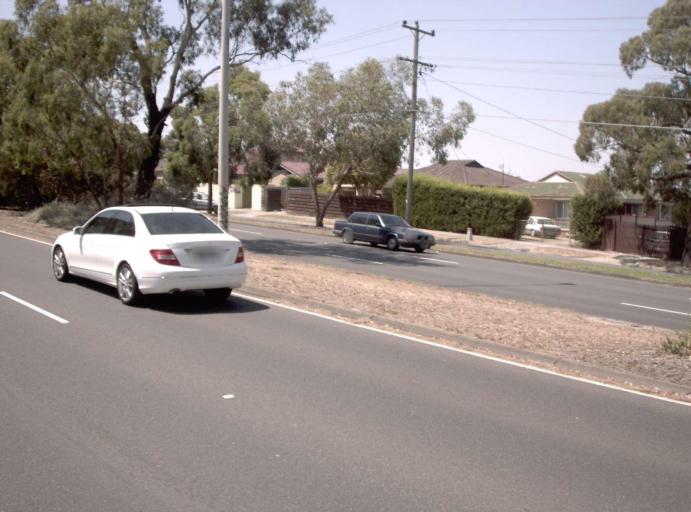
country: AU
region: Victoria
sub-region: Whitehorse
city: Forest Hill
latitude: -37.8503
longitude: 145.1700
